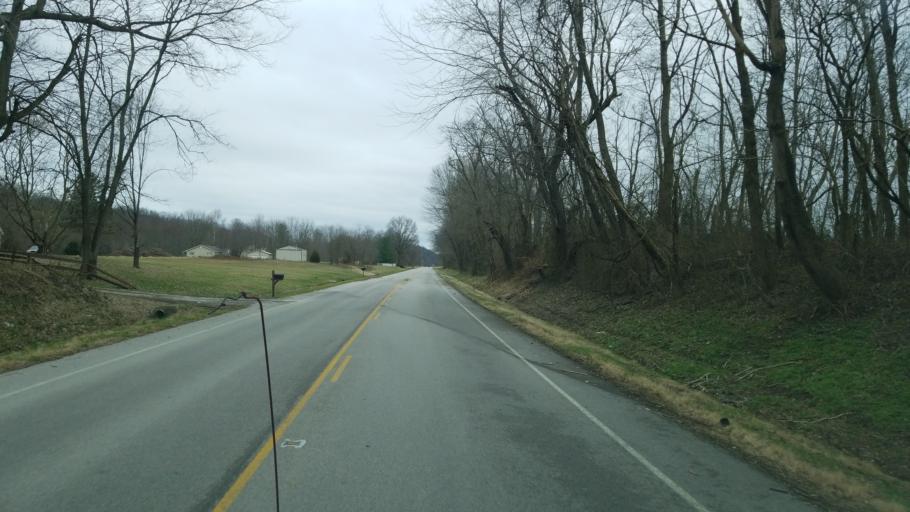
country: US
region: Kentucky
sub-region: Bracken County
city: Augusta
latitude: 38.7874
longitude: -83.9376
